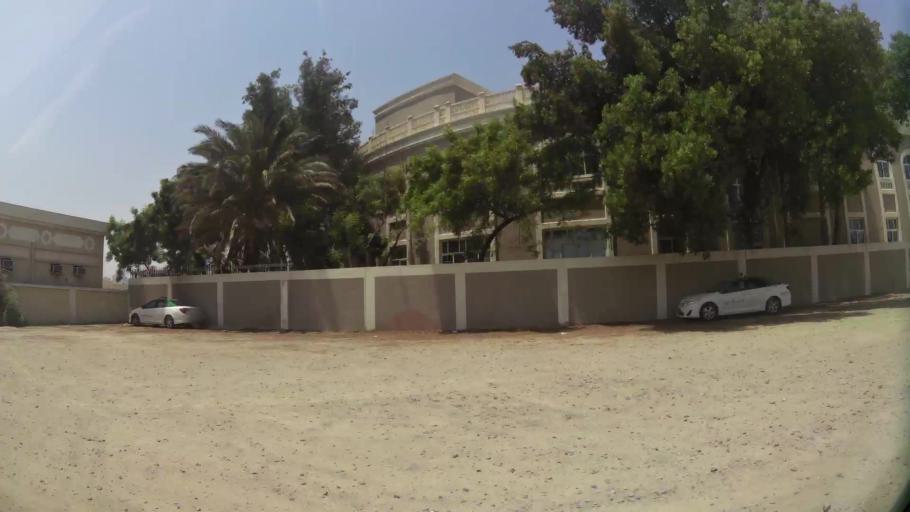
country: AE
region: Ash Shariqah
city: Sharjah
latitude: 25.3453
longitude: 55.3681
